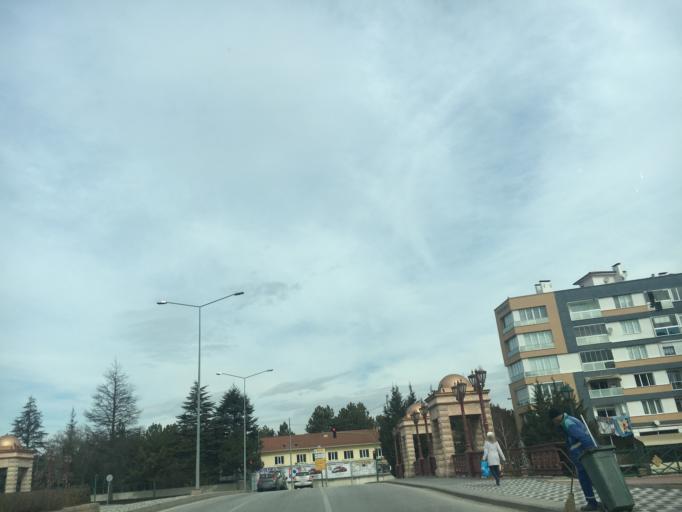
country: TR
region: Eskisehir
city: Eskisehir
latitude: 39.7732
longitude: 30.5009
